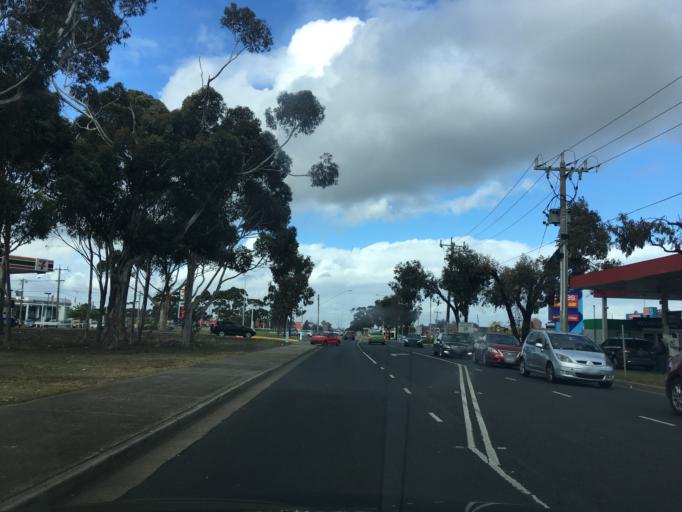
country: AU
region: Victoria
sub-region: Wyndham
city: Hoppers Crossing
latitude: -37.8806
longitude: 144.7038
